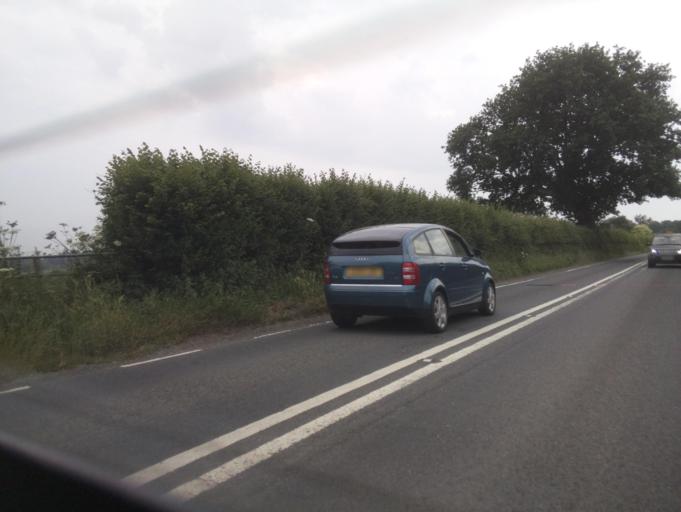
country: GB
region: England
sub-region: Somerset
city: Yeovil
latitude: 50.9234
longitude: -2.6720
